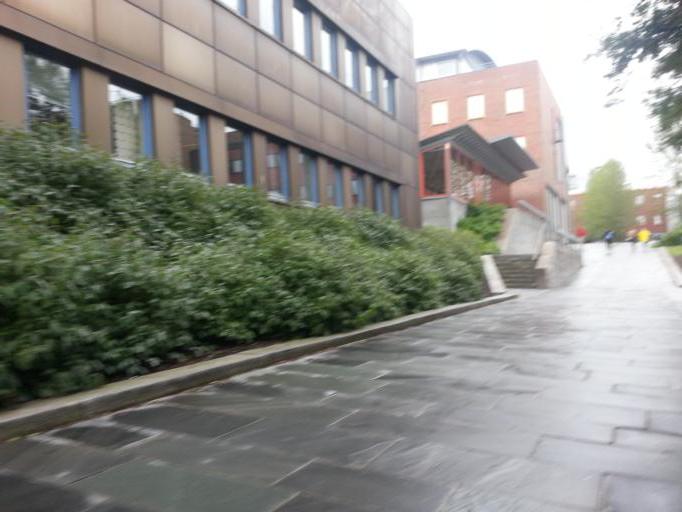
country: NO
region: Troms
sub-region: Tromso
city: Tromso
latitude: 69.6818
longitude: 18.9762
